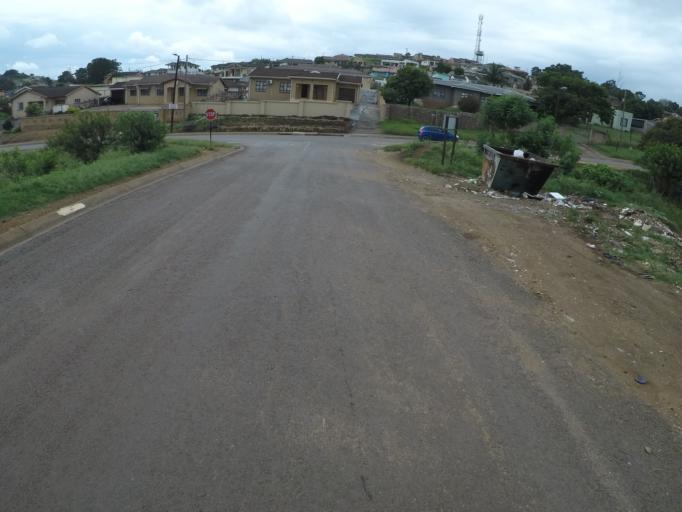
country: ZA
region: KwaZulu-Natal
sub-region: uThungulu District Municipality
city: Empangeni
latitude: -28.7826
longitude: 31.8583
